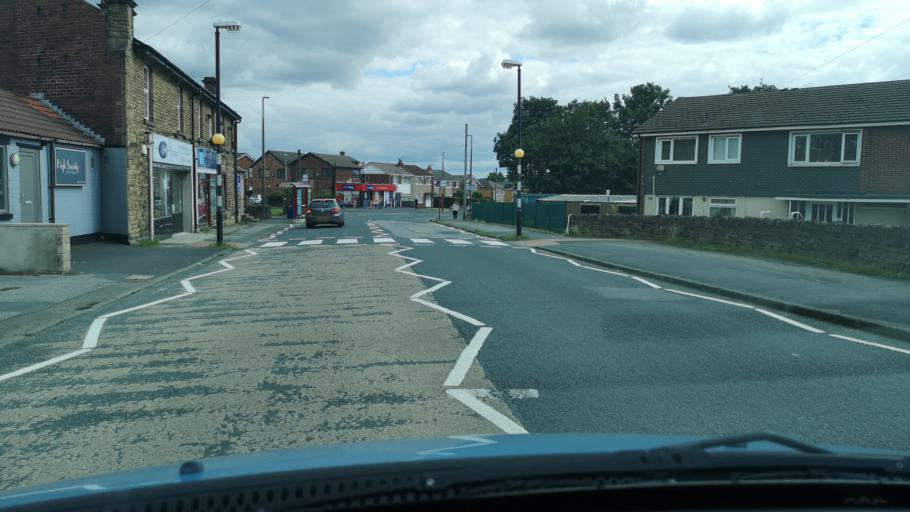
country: GB
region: England
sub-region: Kirklees
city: Mirfield
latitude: 53.6885
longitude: -1.6921
